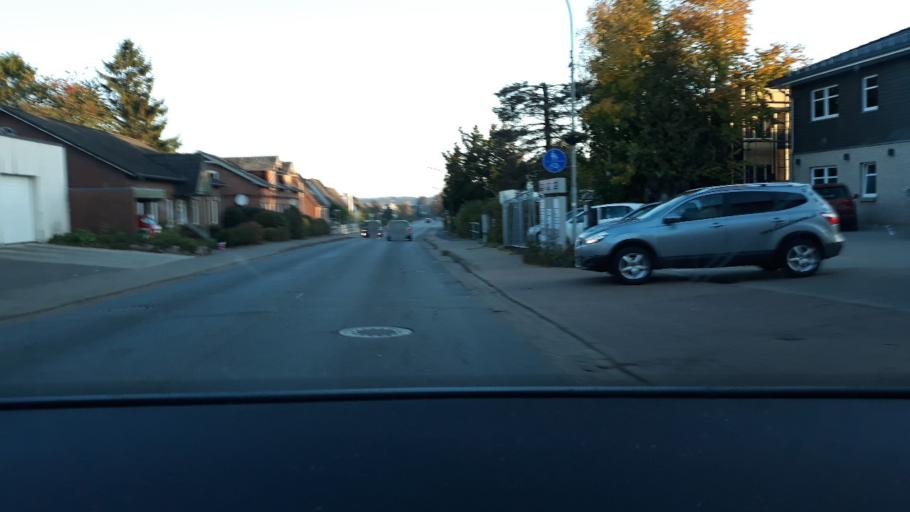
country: DE
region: Schleswig-Holstein
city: Satrup
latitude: 54.6925
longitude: 9.6038
